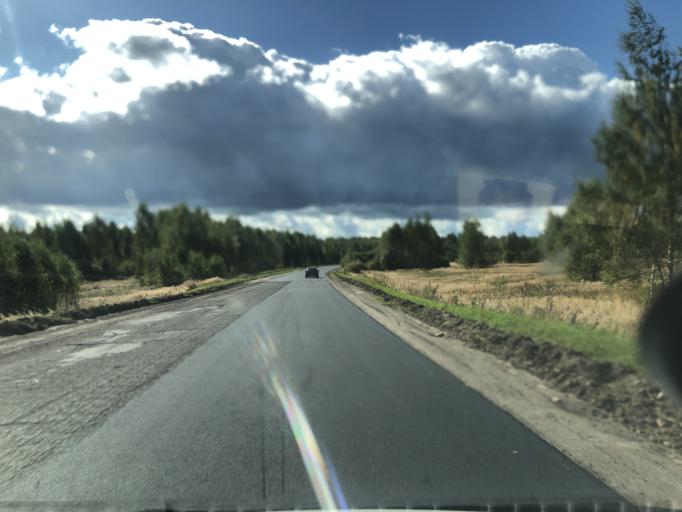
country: RU
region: Jaroslavl
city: Petrovsk
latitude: 56.9674
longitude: 39.3864
